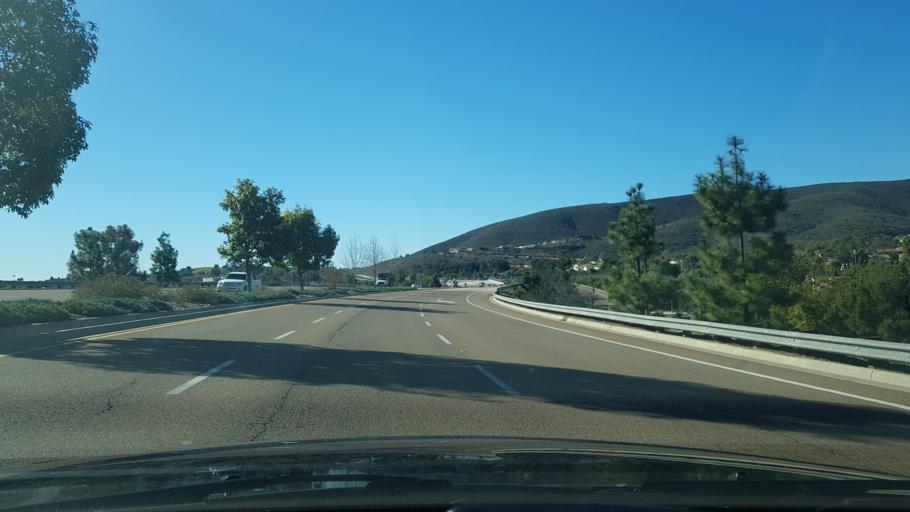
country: US
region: California
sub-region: San Diego County
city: Poway
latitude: 32.9651
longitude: -117.0887
